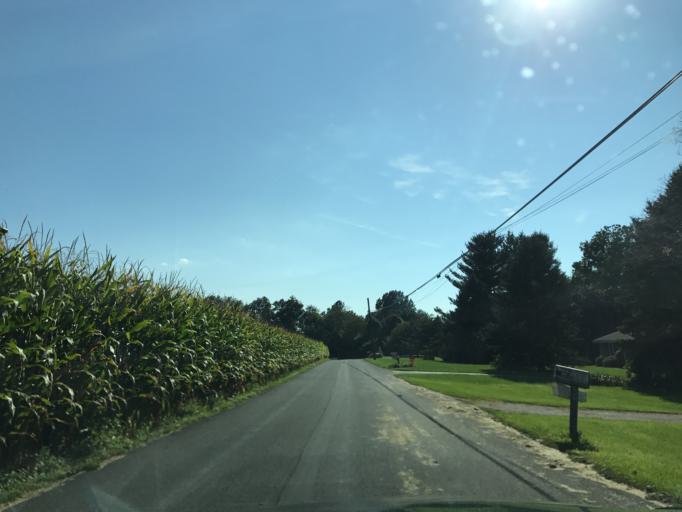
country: US
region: Pennsylvania
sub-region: York County
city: Stewartstown
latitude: 39.6524
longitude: -76.5792
